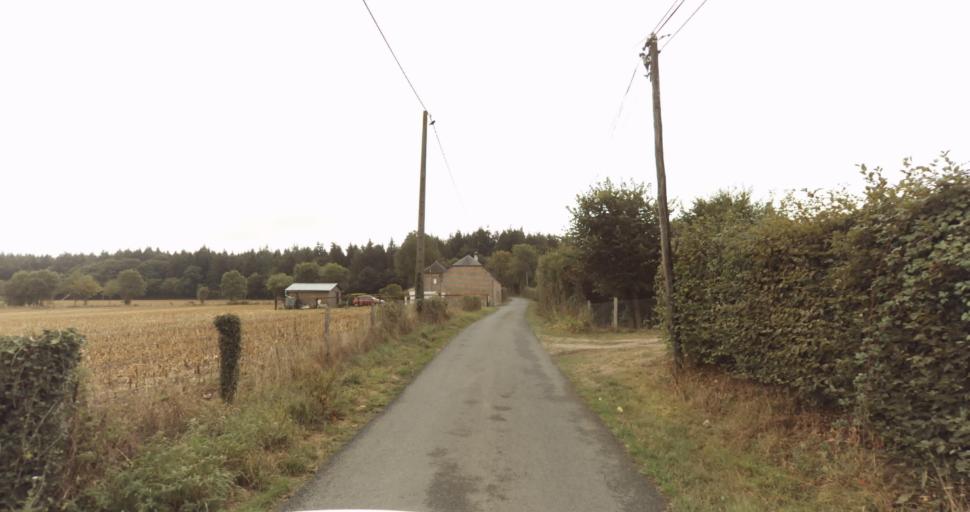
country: FR
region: Lower Normandy
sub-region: Departement de l'Orne
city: Vimoutiers
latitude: 48.9271
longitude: 0.1511
